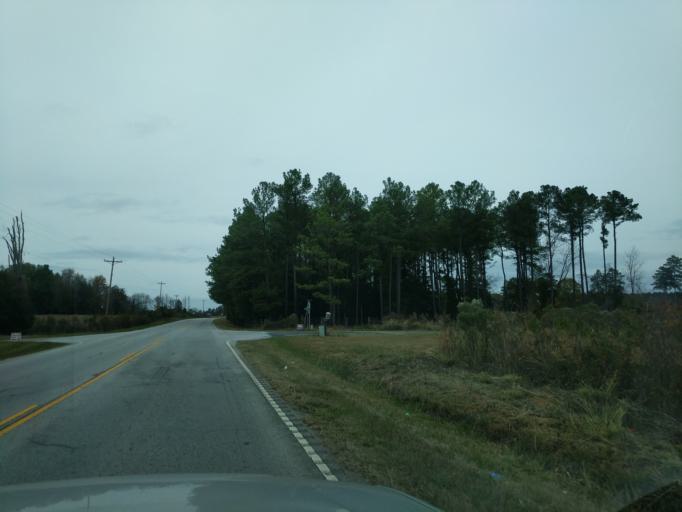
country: US
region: South Carolina
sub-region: Saluda County
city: Saluda
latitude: 34.0357
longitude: -81.7695
